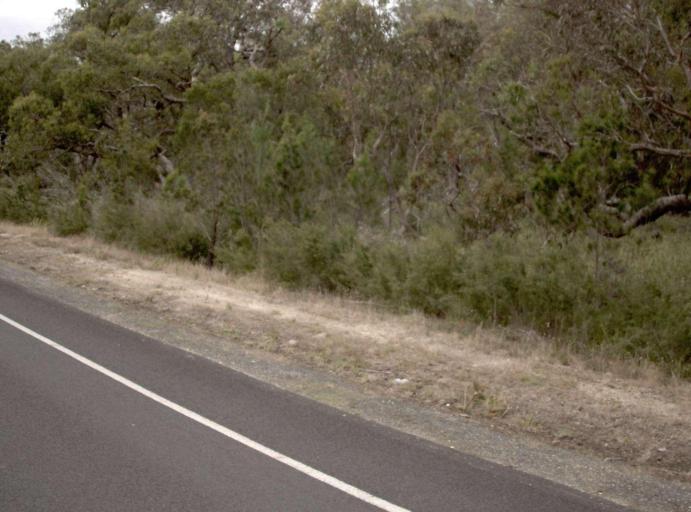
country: AU
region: Victoria
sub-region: Wellington
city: Sale
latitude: -38.2236
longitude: 147.0569
